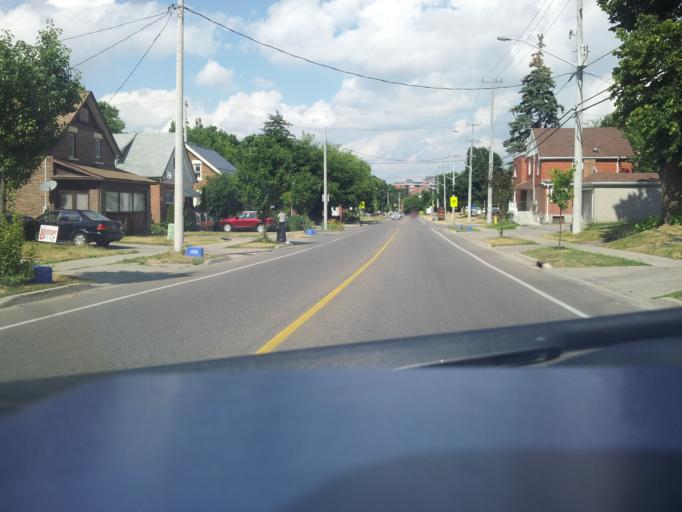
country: CA
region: Ontario
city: Kitchener
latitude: 43.4439
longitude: -80.5097
